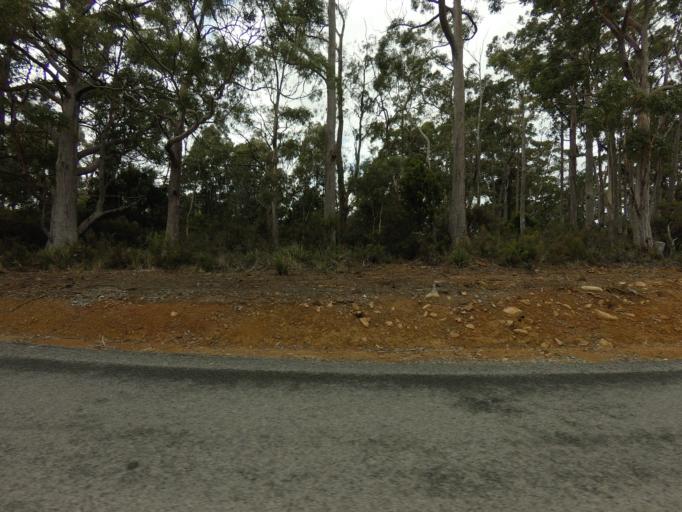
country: AU
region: Tasmania
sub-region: Huon Valley
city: Geeveston
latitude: -43.4331
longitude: 146.9034
